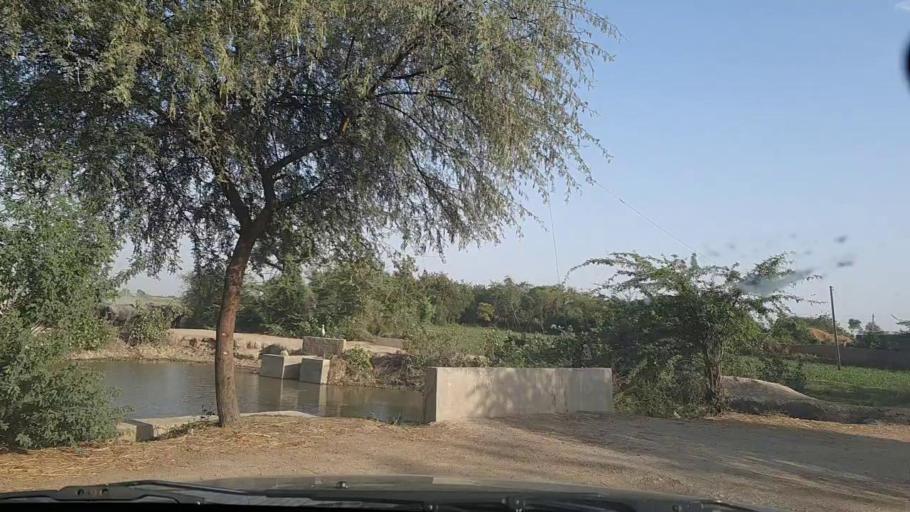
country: PK
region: Sindh
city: Chuhar Jamali
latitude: 24.5522
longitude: 68.1070
